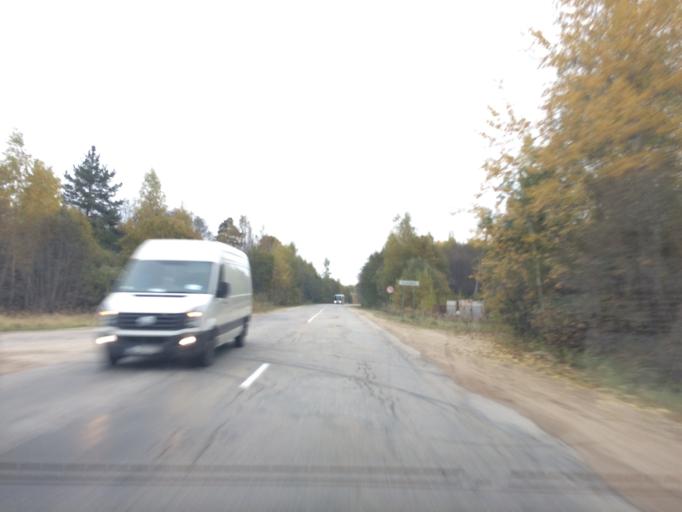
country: LV
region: Plavinu
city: Plavinas
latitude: 56.6053
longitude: 25.6787
